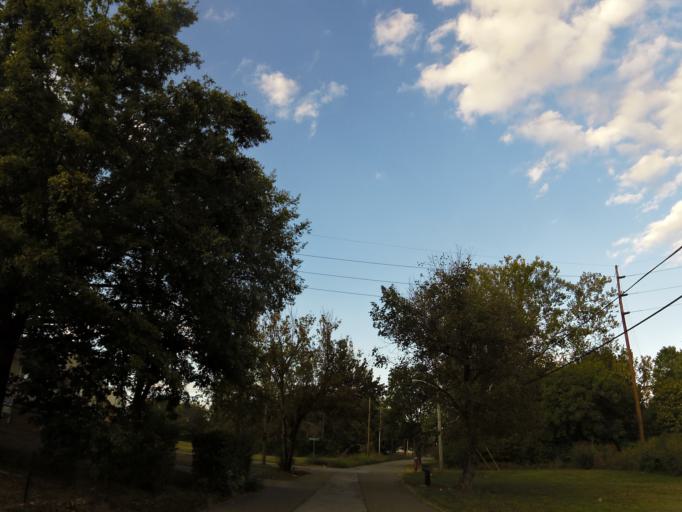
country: US
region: Tennessee
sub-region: Knox County
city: Knoxville
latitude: 36.0254
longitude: -83.9217
